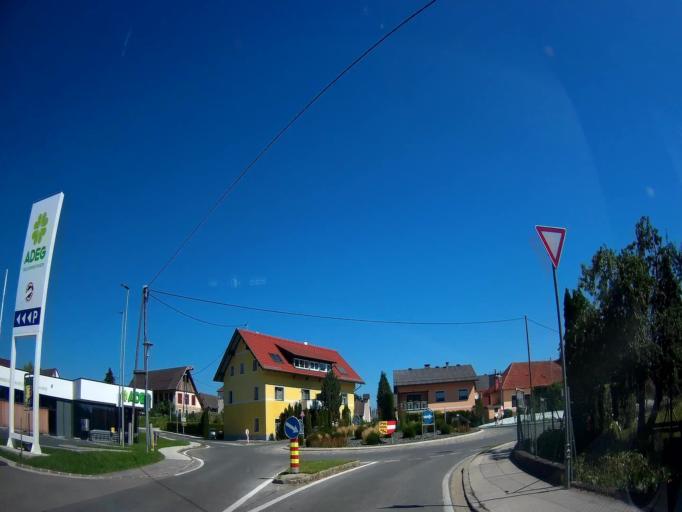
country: AT
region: Carinthia
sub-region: Politischer Bezirk Klagenfurt Land
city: Ebenthal
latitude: 46.6079
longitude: 14.3987
